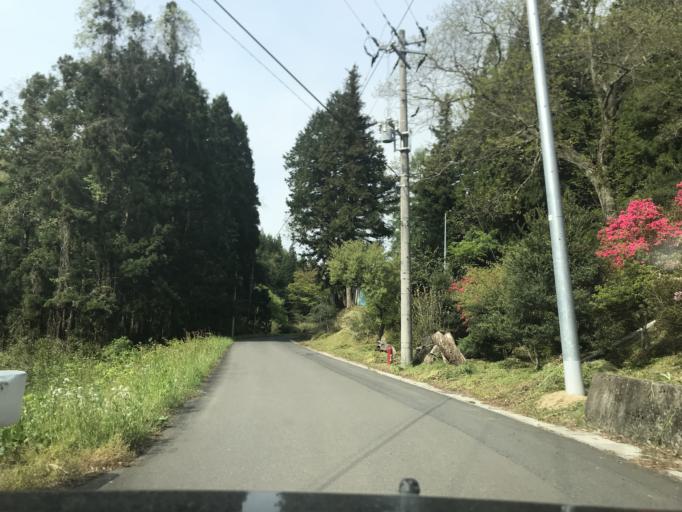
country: JP
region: Iwate
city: Ichinoseki
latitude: 38.9076
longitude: 141.0600
